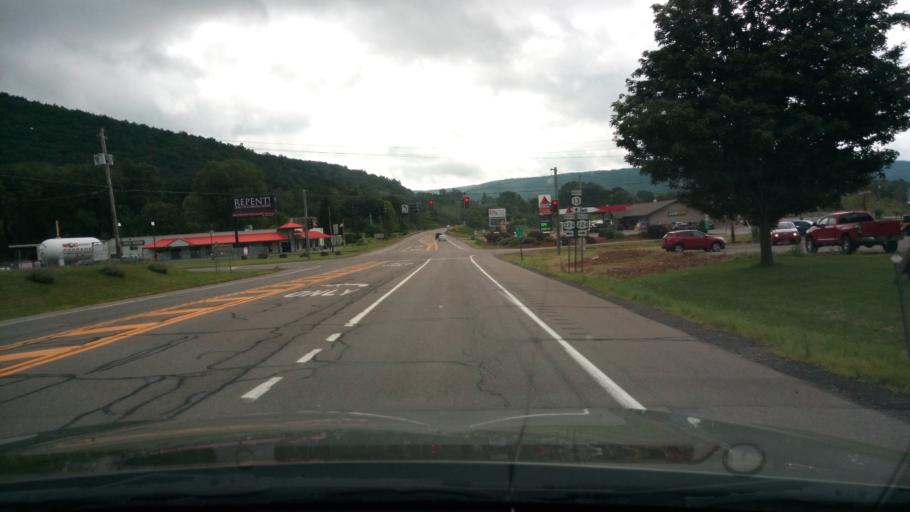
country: US
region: New York
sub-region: Chemung County
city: Horseheads North
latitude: 42.2937
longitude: -76.7162
